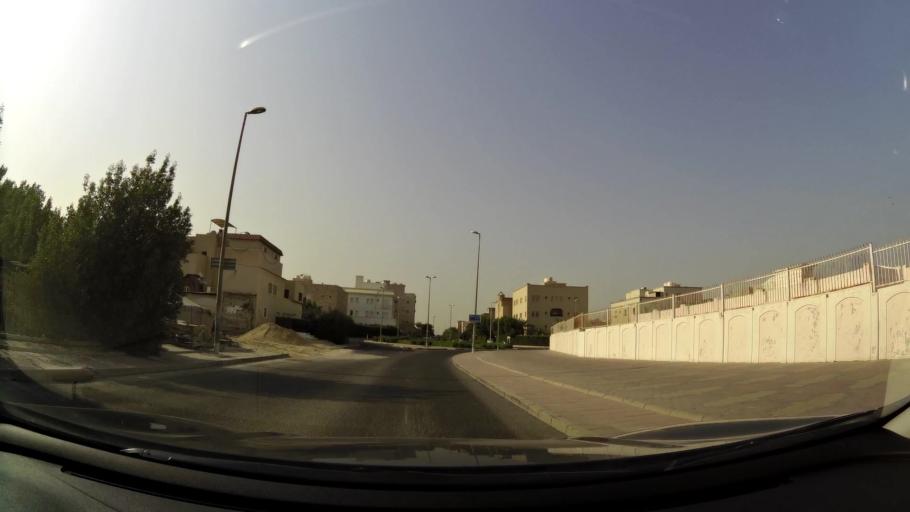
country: KW
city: Al Funaytis
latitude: 29.2193
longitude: 48.0822
